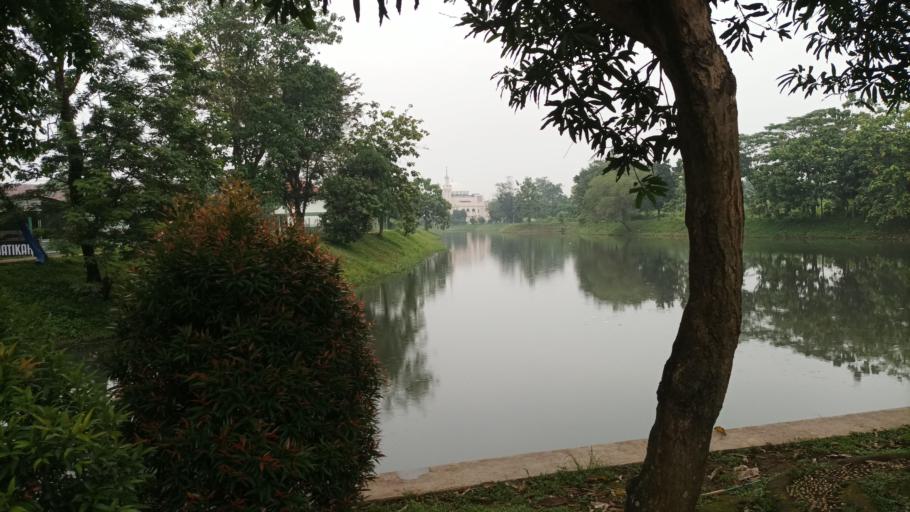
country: ID
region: West Java
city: Cileungsir
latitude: -6.3896
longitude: 106.9158
